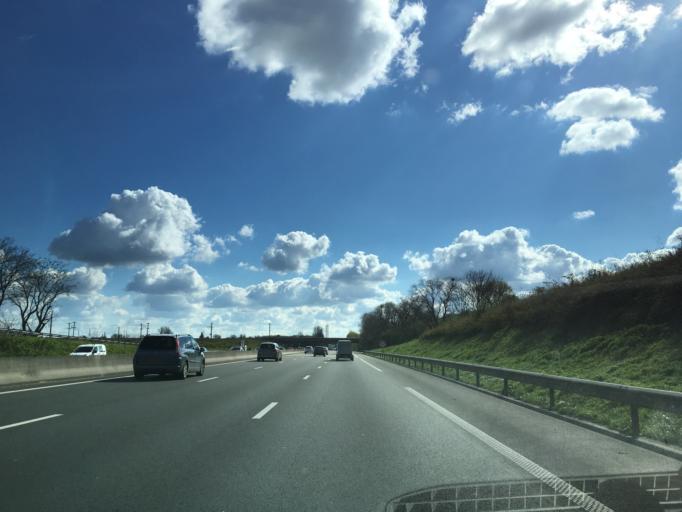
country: FR
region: Nord-Pas-de-Calais
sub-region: Departement du Nord
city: Attiches
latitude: 50.5446
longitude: 3.0556
